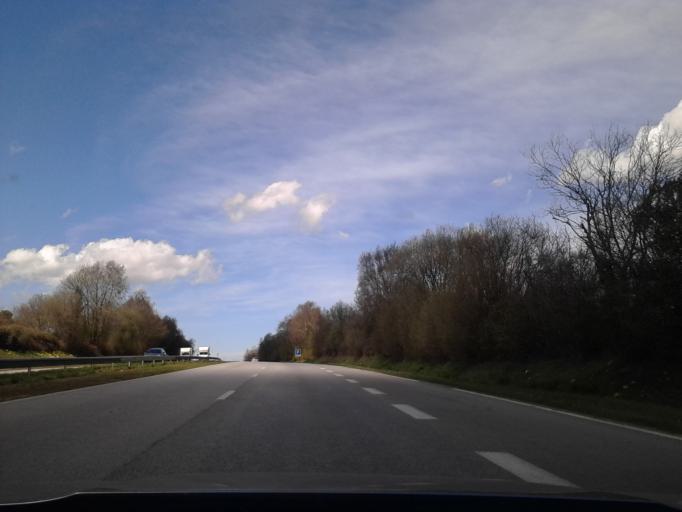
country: FR
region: Lower Normandy
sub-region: Departement de la Manche
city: Brix
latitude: 49.5653
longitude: -1.5698
